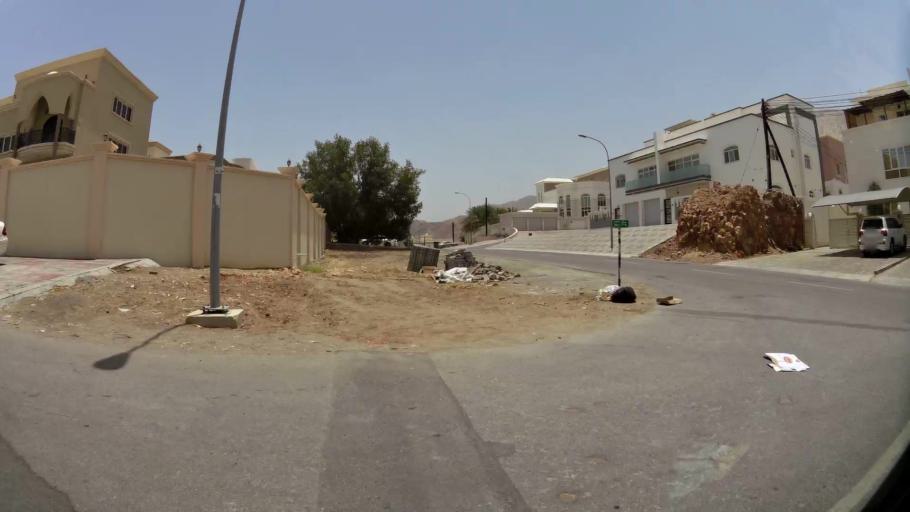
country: OM
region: Muhafazat Masqat
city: Bawshar
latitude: 23.5594
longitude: 58.4109
